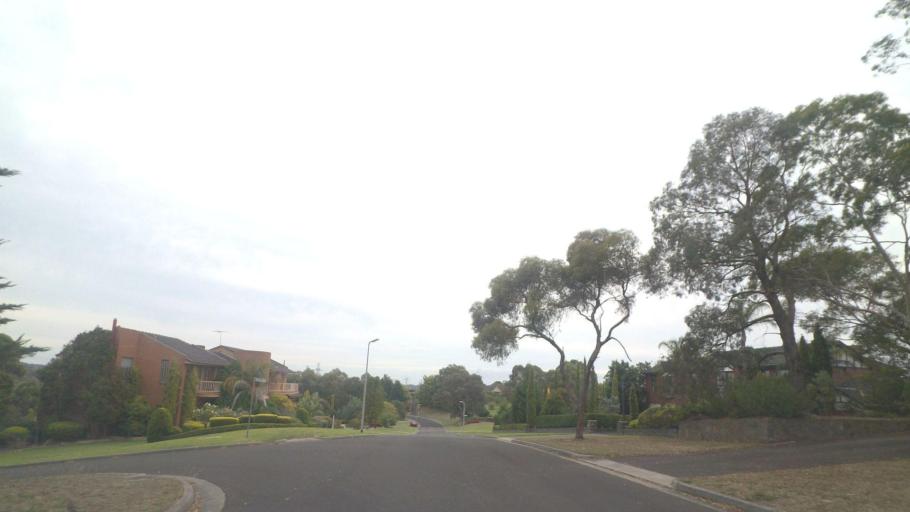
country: AU
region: Victoria
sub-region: Manningham
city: Park Orchards
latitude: -37.7549
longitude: 145.1925
